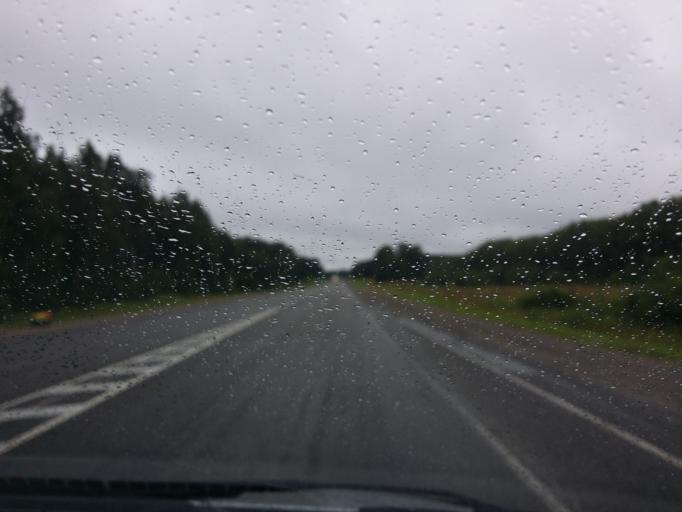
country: RU
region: Altai Krai
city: Troitskoye
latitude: 53.0516
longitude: 84.6923
